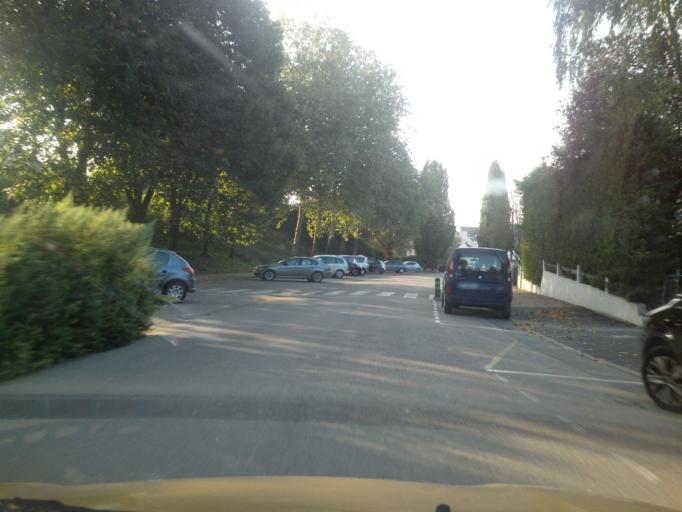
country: FR
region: Brittany
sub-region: Departement du Morbihan
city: Ploermel
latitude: 47.9337
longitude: -2.3963
